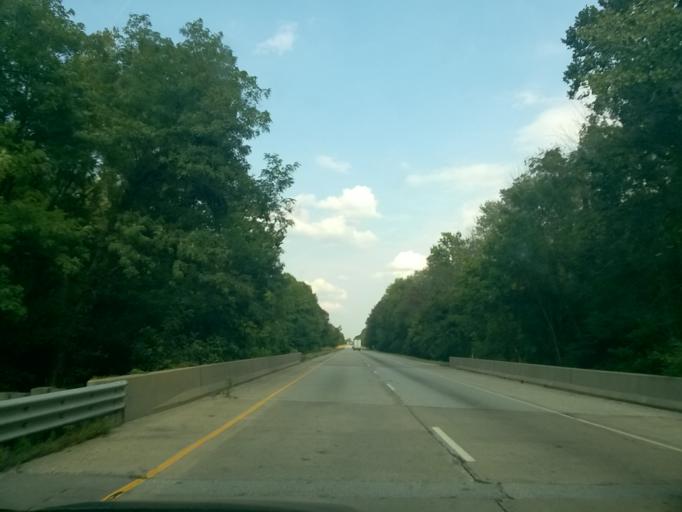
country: US
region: Indiana
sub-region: Vigo County
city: Seelyville
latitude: 39.4433
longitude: -87.2675
